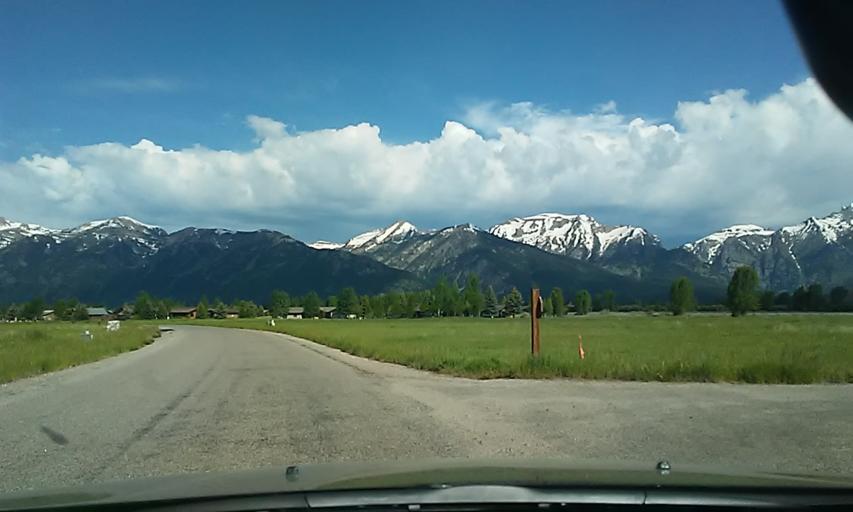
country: US
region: Wyoming
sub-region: Teton County
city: Jackson
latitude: 43.5772
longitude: -110.7470
